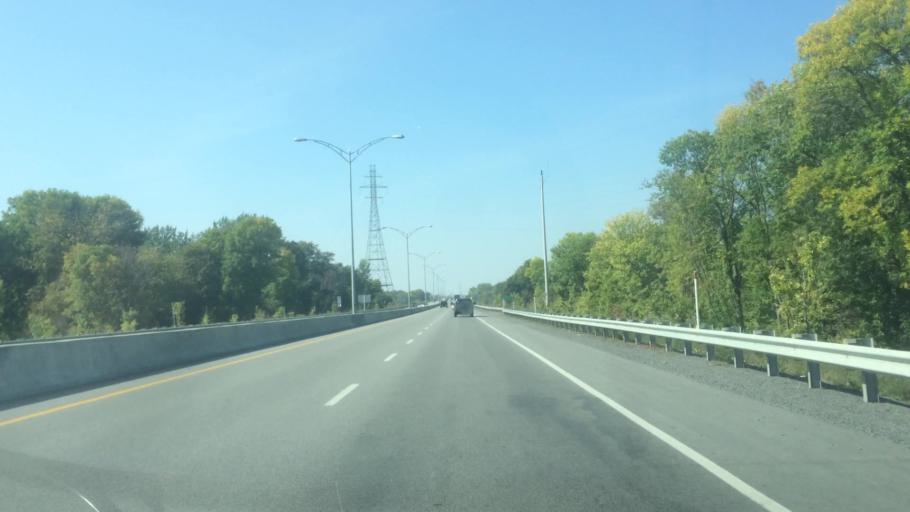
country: CA
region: Quebec
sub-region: Monteregie
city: Salaberry-de-Valleyfield
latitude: 45.2706
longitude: -74.1712
